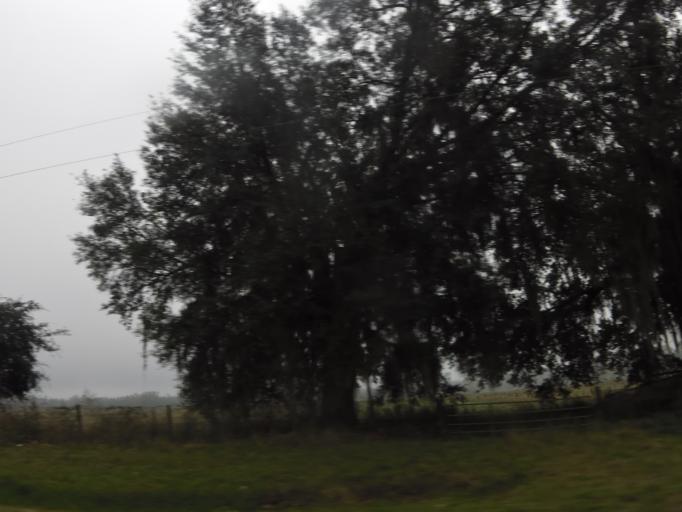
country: US
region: Florida
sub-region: Alachua County
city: Alachua
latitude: 29.8847
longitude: -82.4510
